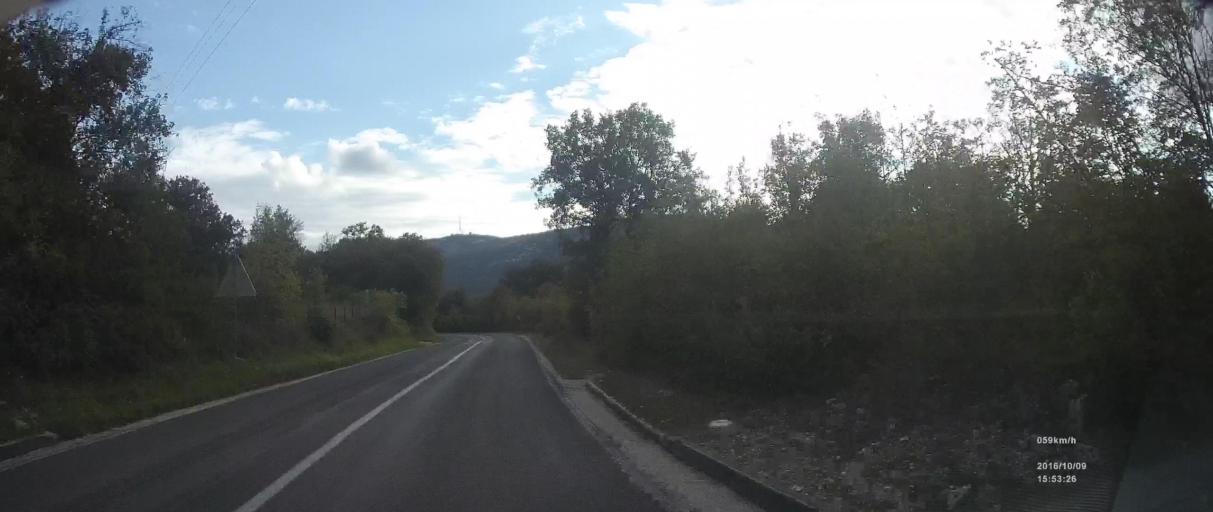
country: HR
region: Splitsko-Dalmatinska
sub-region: Grad Trogir
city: Trogir
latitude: 43.6054
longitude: 16.2248
